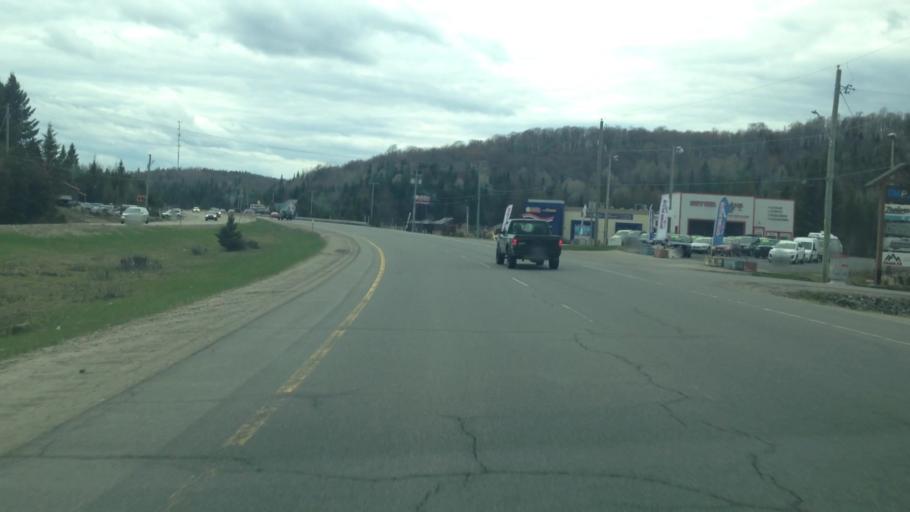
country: CA
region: Quebec
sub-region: Laurentides
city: Sainte-Agathe-des-Monts
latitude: 46.0772
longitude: -74.3141
